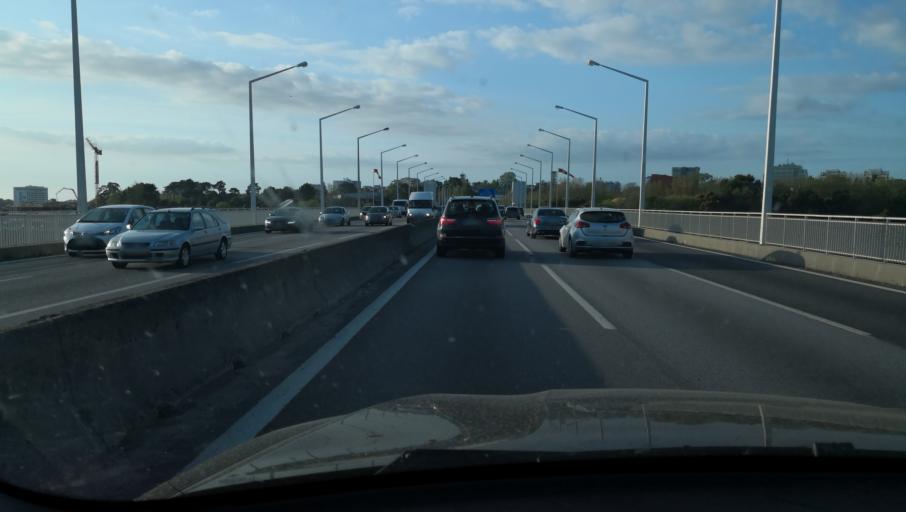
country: PT
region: Porto
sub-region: Vila Nova de Gaia
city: Canidelo
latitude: 41.1465
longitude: -8.6400
